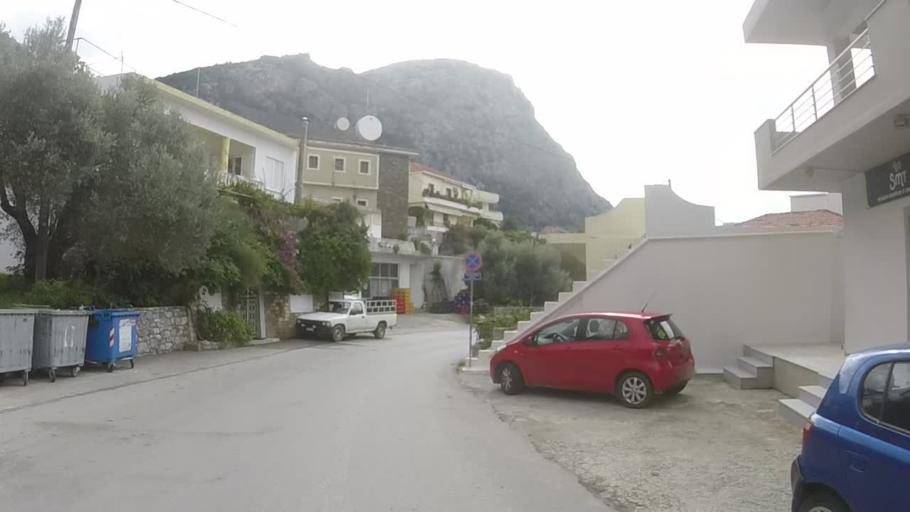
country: GR
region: Crete
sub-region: Nomos Rethymnis
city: Agia Foteini
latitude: 35.2198
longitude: 24.5338
